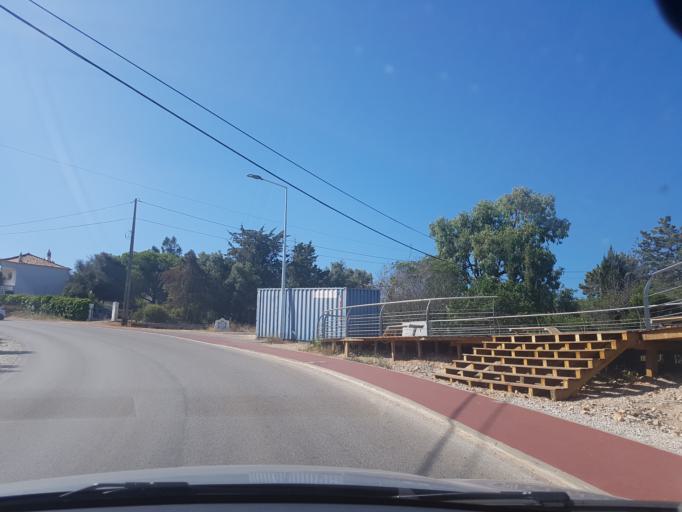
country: PT
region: Faro
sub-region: Lagoa
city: Carvoeiro
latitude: 37.0946
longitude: -8.4572
